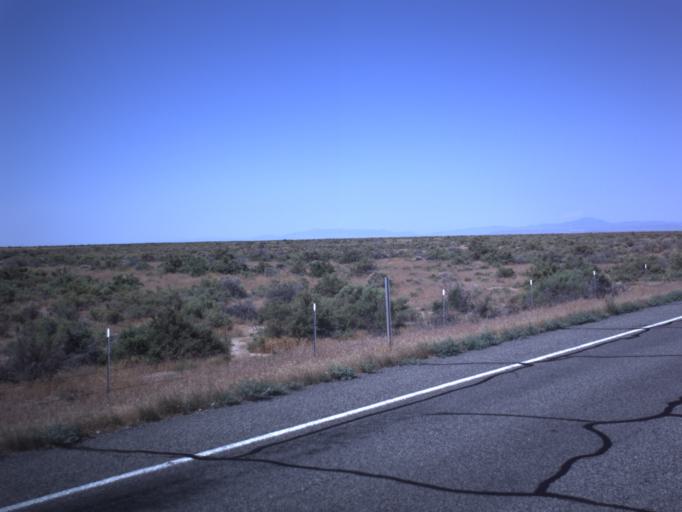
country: US
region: Utah
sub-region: Millard County
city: Delta
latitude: 39.4695
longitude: -112.4569
